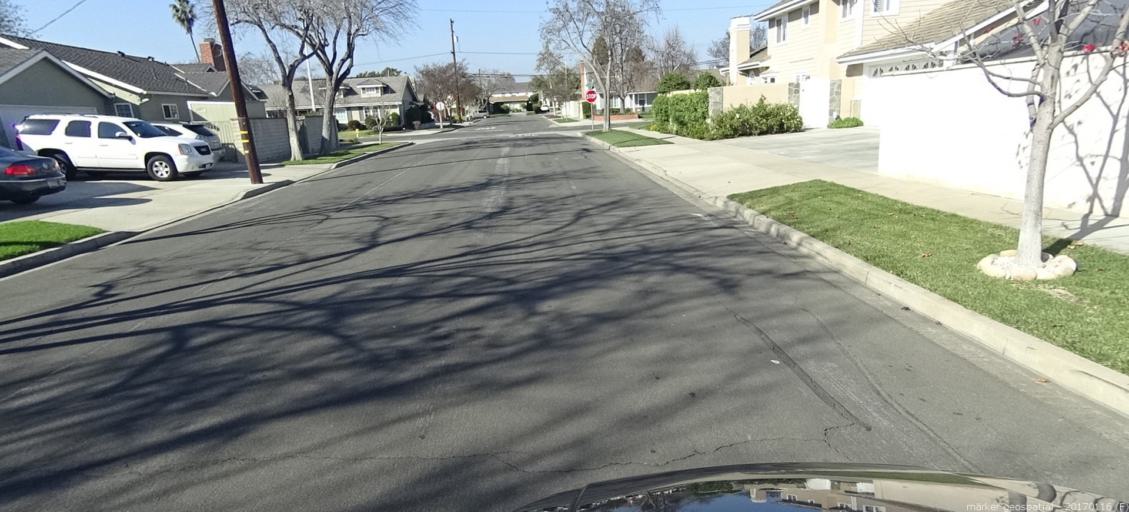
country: US
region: California
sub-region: Orange County
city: Rossmoor
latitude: 33.7889
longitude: -118.0806
